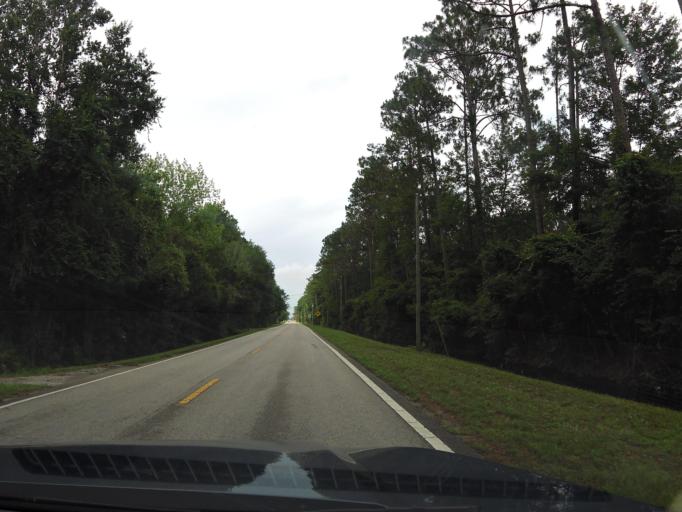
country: US
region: Florida
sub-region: Saint Johns County
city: Saint Augustine South
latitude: 29.8581
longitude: -81.4262
